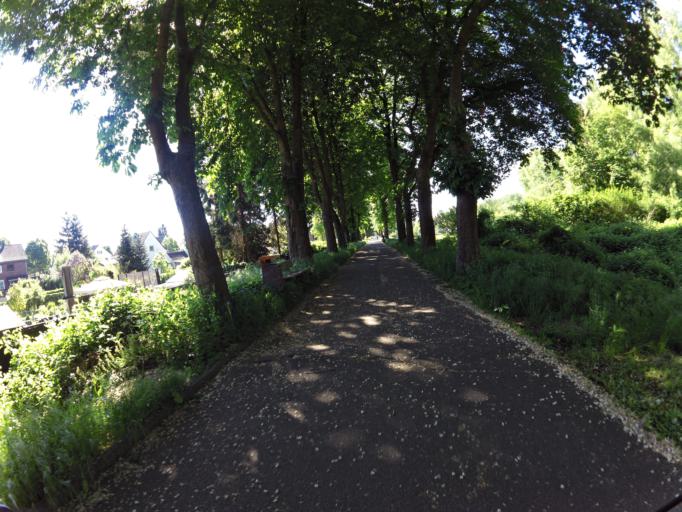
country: DE
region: North Rhine-Westphalia
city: Julich
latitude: 50.9131
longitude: 6.3549
